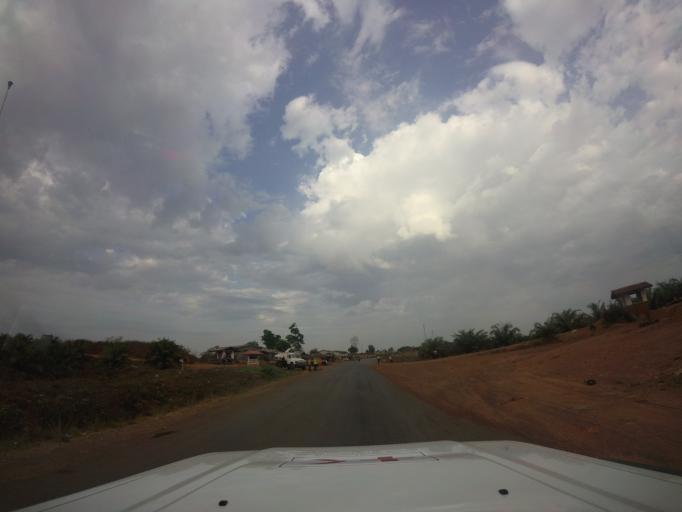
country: LR
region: Bomi
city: Tubmanburg
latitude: 6.7126
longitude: -10.9671
